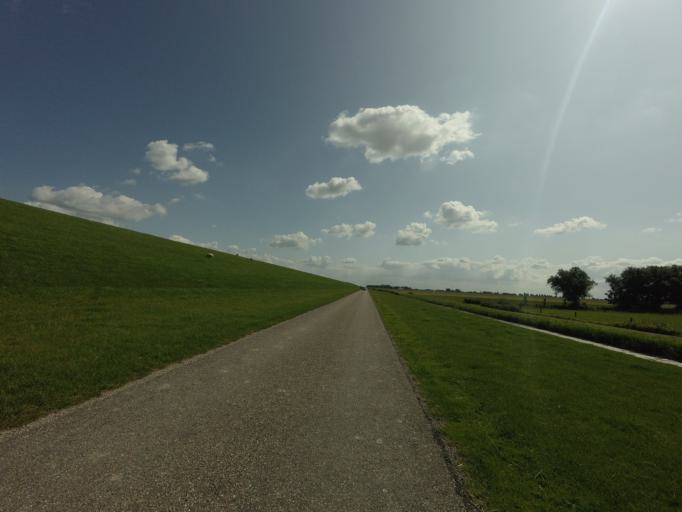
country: NL
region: Friesland
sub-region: Gemeente Ferwerderadiel
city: Hallum
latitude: 53.3223
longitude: 5.7429
